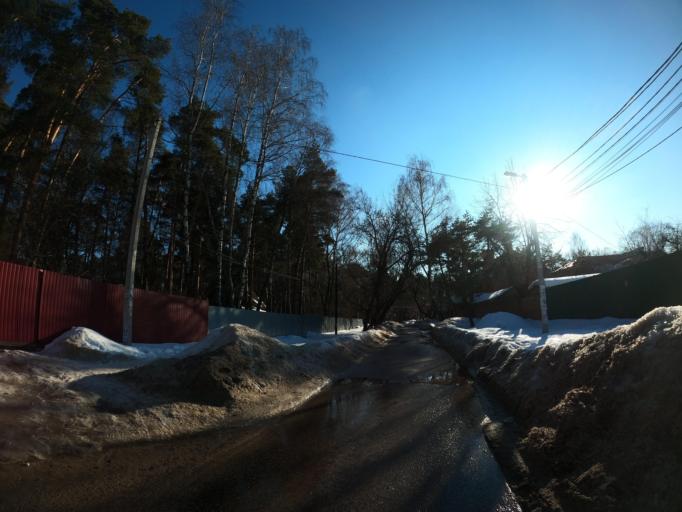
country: RU
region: Moskovskaya
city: Kraskovo
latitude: 55.6411
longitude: 37.9935
